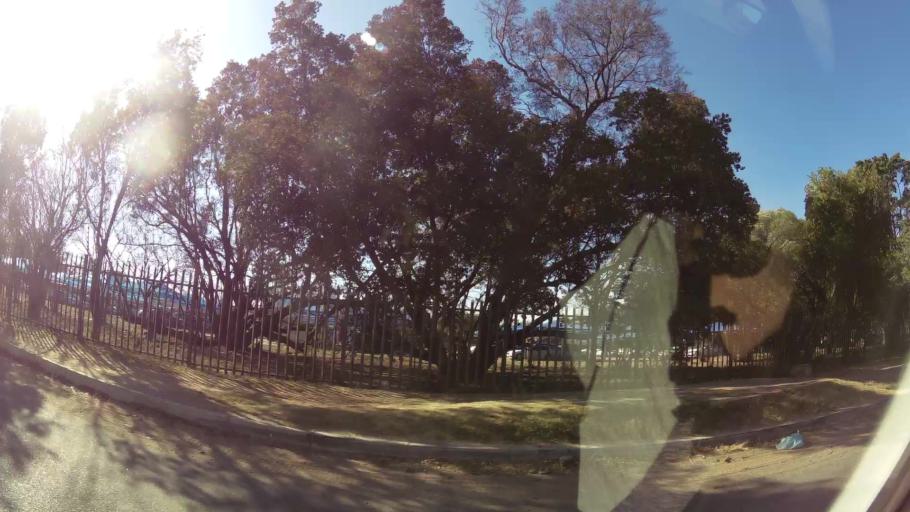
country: ZA
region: Gauteng
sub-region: Ekurhuleni Metropolitan Municipality
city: Germiston
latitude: -26.2274
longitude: 28.1151
